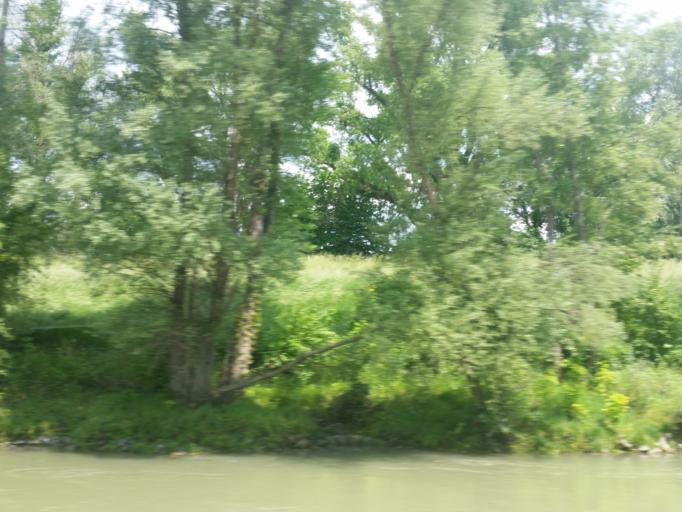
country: AT
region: Lower Austria
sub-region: Politischer Bezirk Wien-Umgebung
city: Schwechat
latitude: 48.1802
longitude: 16.4536
